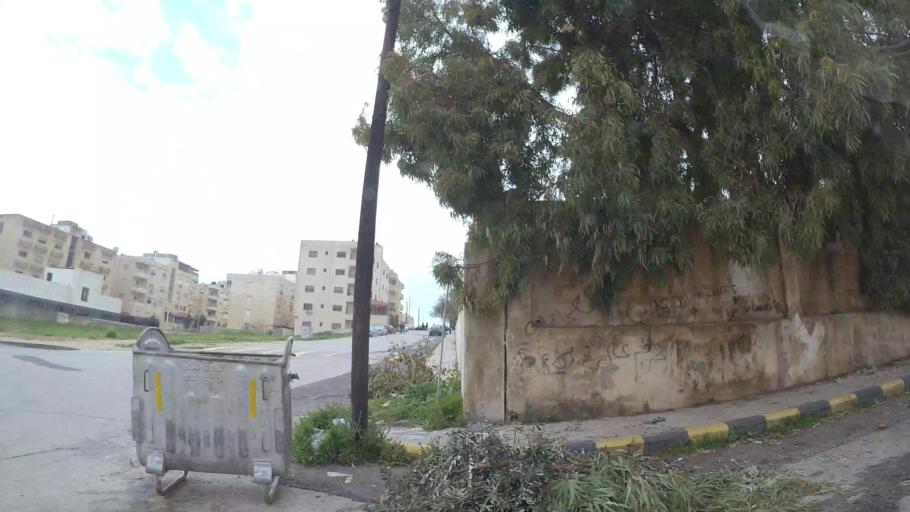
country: JO
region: Amman
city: Umm as Summaq
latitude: 31.8955
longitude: 35.8443
